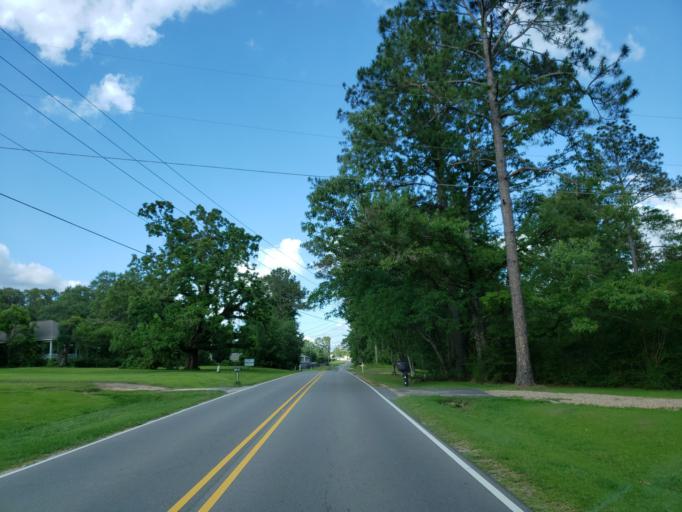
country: US
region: Mississippi
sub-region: Lamar County
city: West Hattiesburg
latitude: 31.2835
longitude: -89.4263
